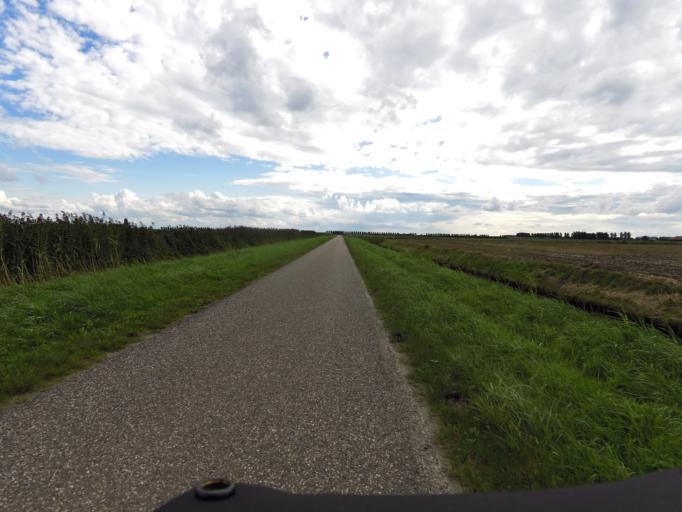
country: NL
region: South Holland
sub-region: Gemeente Goeree-Overflakkee
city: Middelharnis
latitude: 51.7112
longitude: 4.2431
